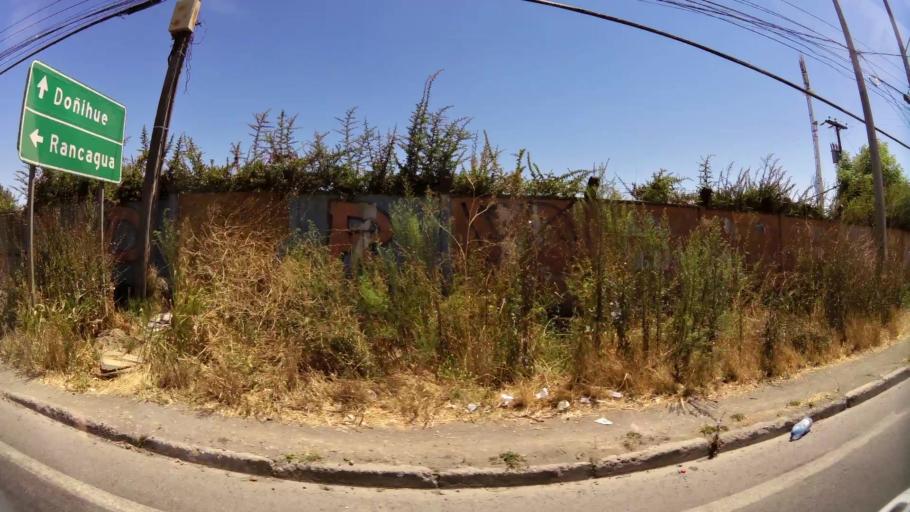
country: CL
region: O'Higgins
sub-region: Provincia de Cachapoal
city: Rancagua
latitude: -34.1550
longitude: -70.7681
